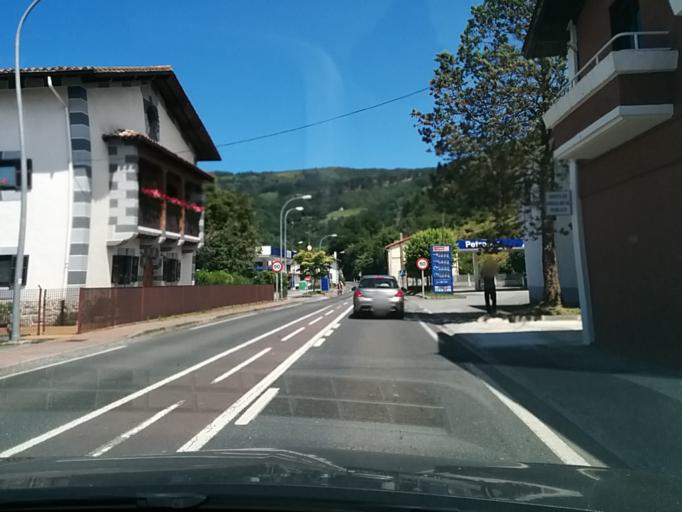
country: ES
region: Basque Country
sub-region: Provincia de Guipuzcoa
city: Usurbil
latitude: 43.2775
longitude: -2.0727
